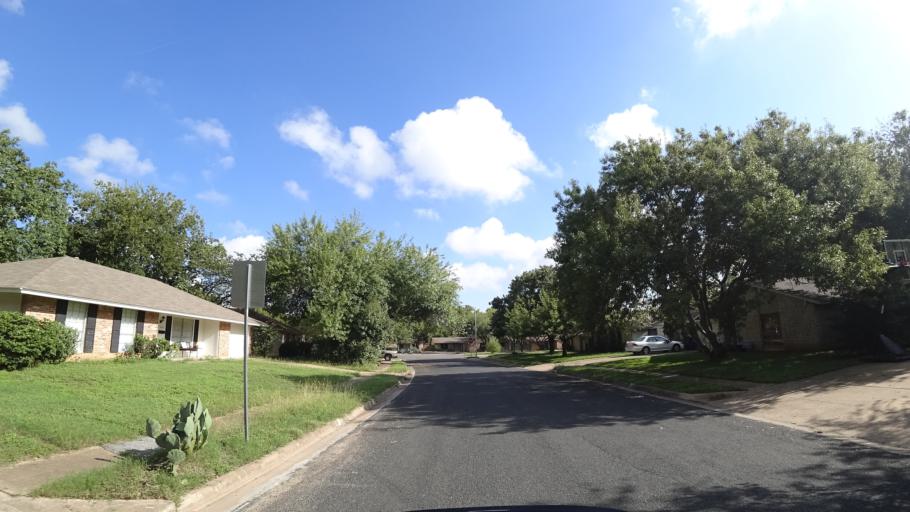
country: US
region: Texas
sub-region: Travis County
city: Rollingwood
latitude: 30.2176
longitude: -97.8021
